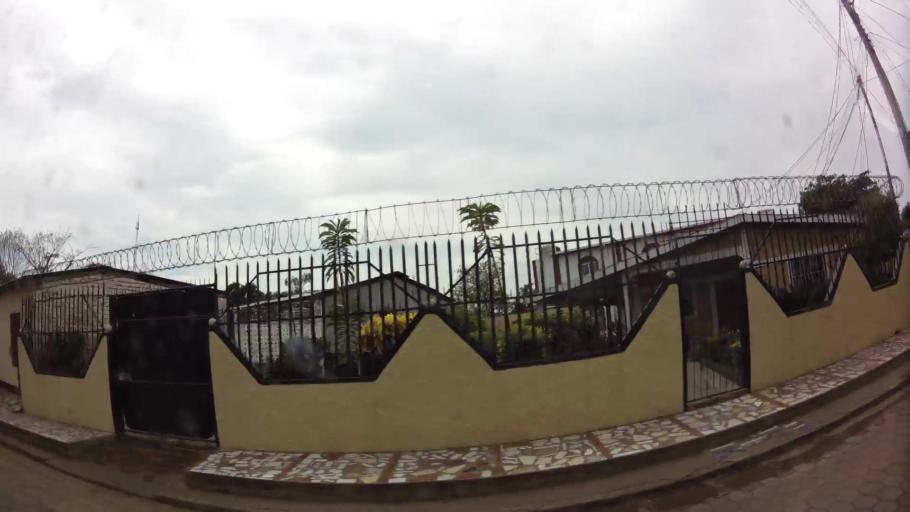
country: NI
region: Rivas
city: Rivas
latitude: 11.4367
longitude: -85.8260
